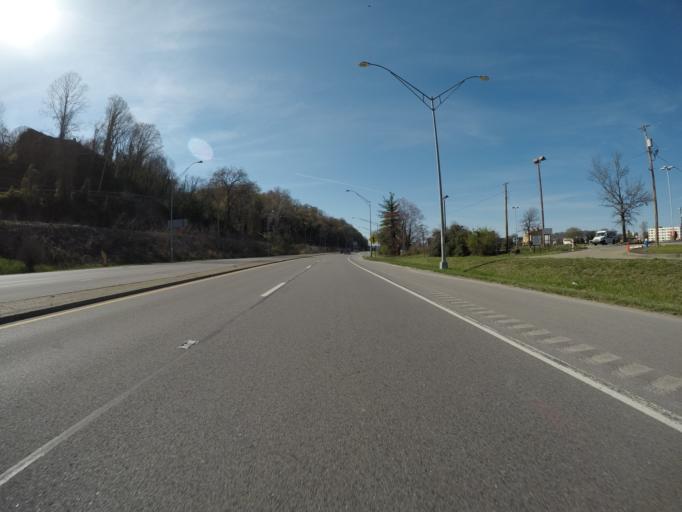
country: US
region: West Virginia
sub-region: Kanawha County
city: Charleston
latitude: 38.3386
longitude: -81.6296
